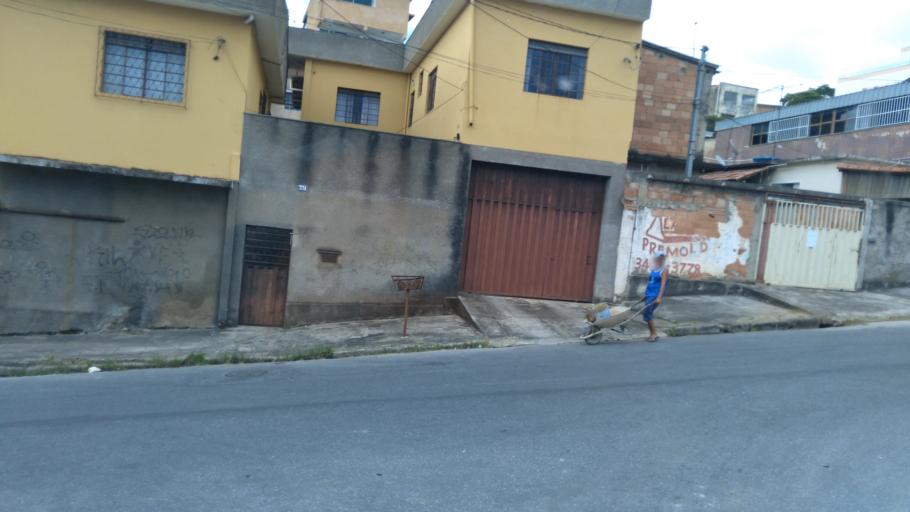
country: BR
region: Minas Gerais
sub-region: Belo Horizonte
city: Belo Horizonte
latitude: -19.8609
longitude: -43.9135
